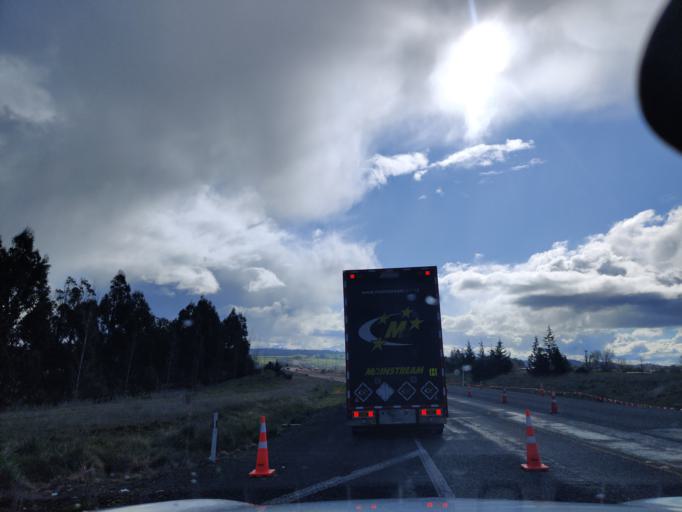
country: NZ
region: Waikato
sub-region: Taupo District
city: Taupo
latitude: -38.6710
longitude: 176.1119
